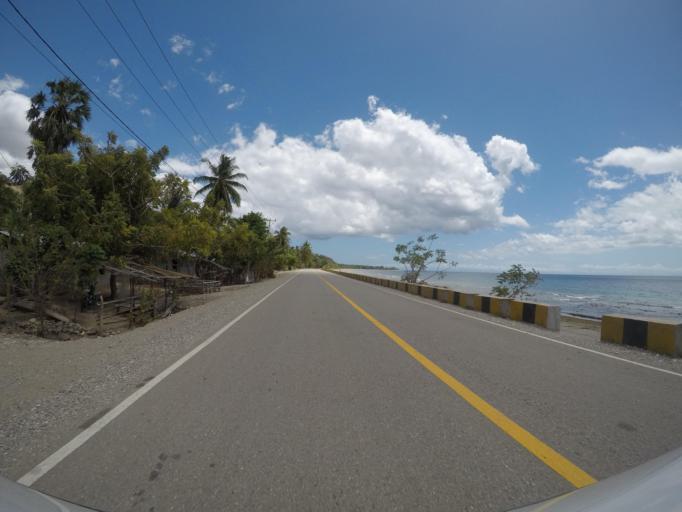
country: TL
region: Lautem
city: Lospalos
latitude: -8.4194
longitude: 126.7540
